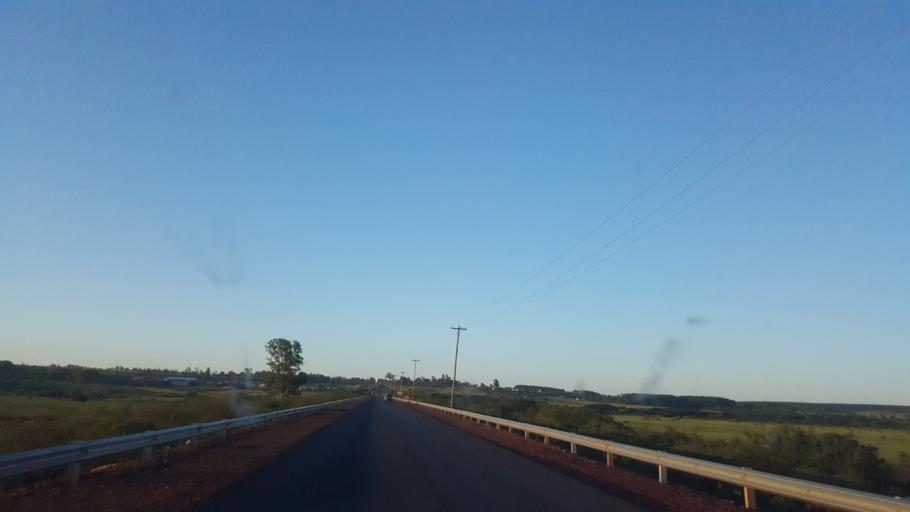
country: AR
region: Corrientes
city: Santo Tome
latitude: -28.5365
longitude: -56.0515
